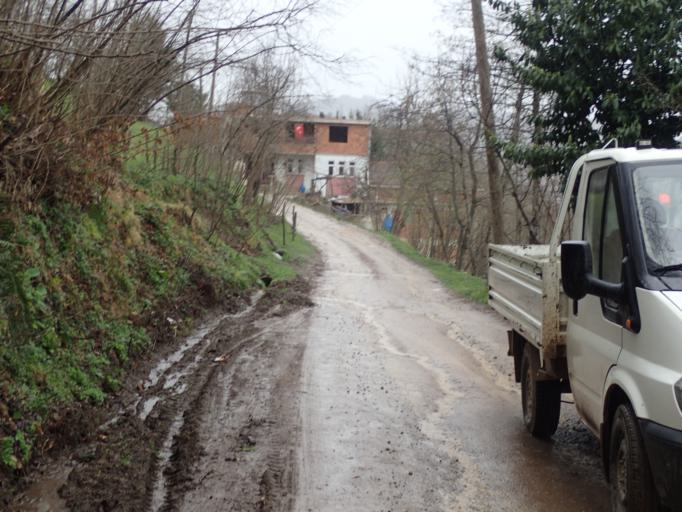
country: TR
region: Ordu
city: Camas
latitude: 40.8831
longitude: 37.4983
